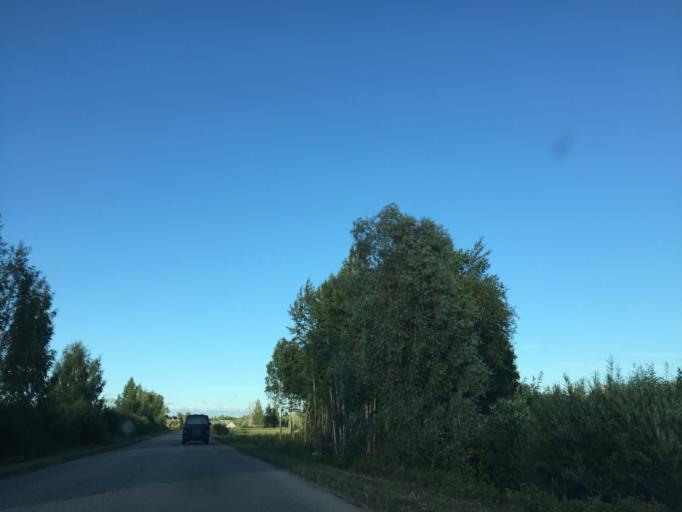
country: LV
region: Plavinu
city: Plavinas
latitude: 56.6092
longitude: 25.8298
